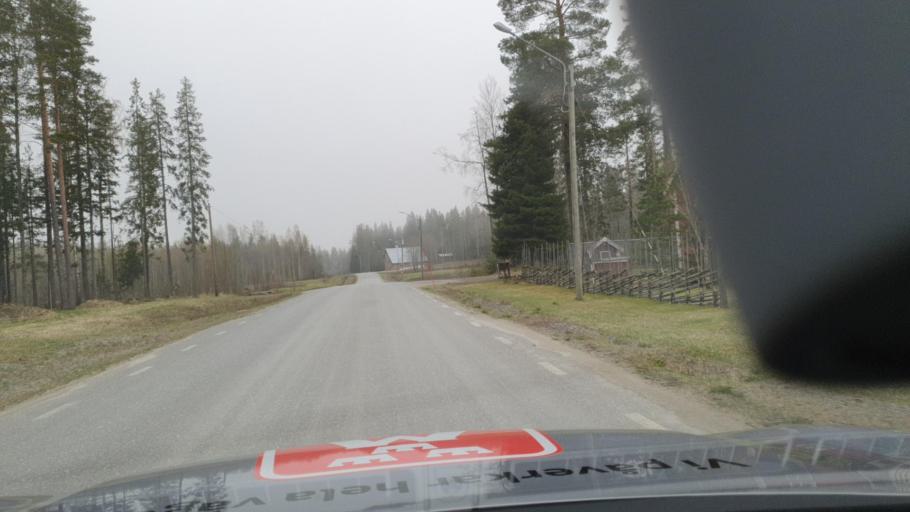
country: SE
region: Vaesternorrland
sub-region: OErnskoeldsviks Kommun
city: Husum
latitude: 63.5925
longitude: 19.0161
